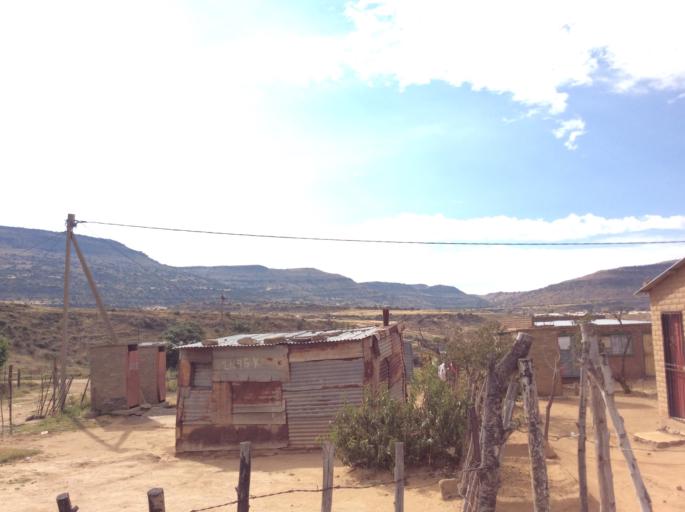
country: LS
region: Mafeteng
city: Mafeteng
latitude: -29.7176
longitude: 27.0173
